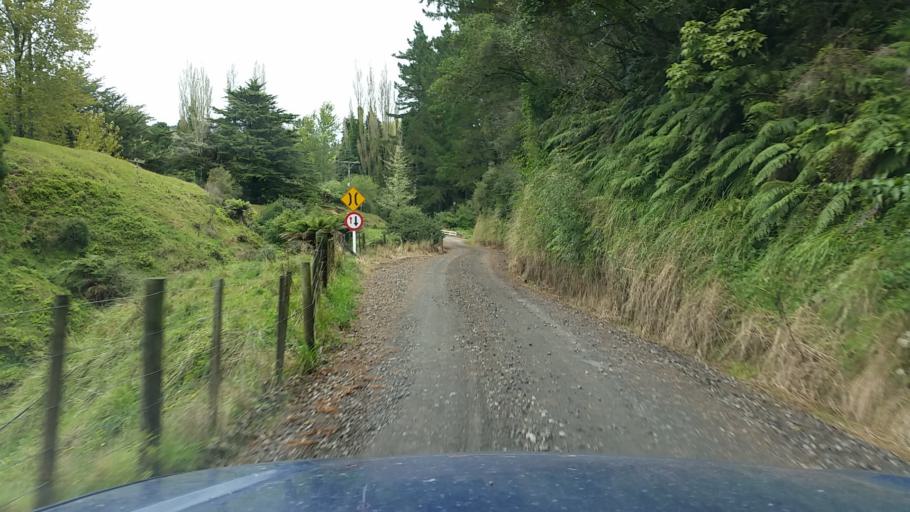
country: NZ
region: Taranaki
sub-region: South Taranaki District
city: Eltham
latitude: -39.2643
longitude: 174.4134
